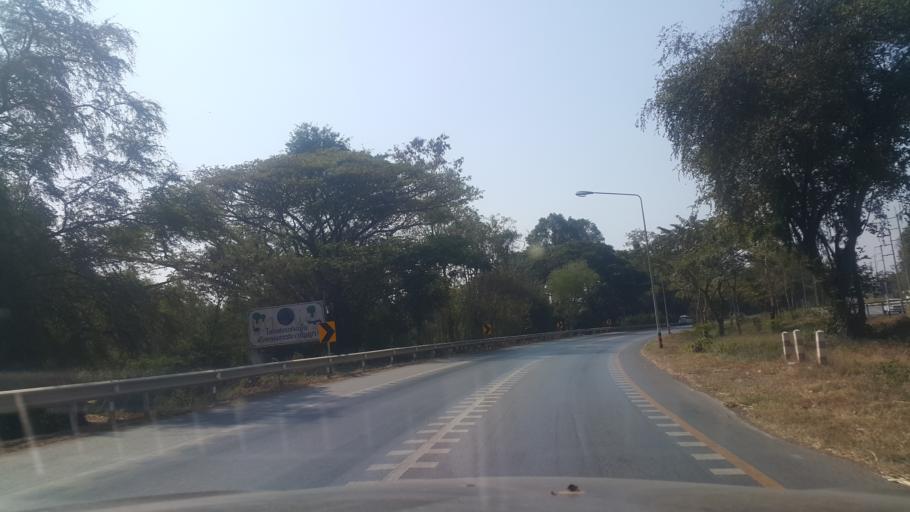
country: TH
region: Nakhon Ratchasima
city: Pak Thong Chai
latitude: 14.6031
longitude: 102.0083
